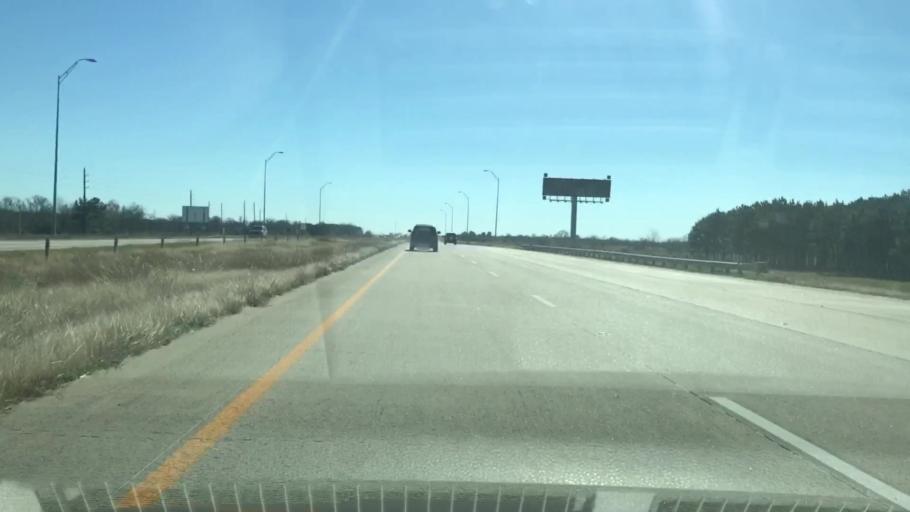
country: US
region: Texas
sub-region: Harris County
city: Cypress
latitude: 29.9003
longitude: -95.7584
